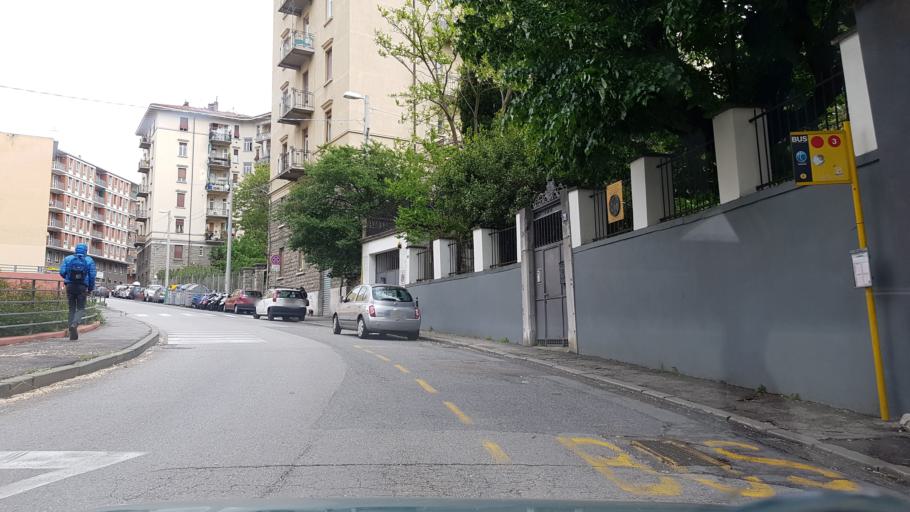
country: IT
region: Friuli Venezia Giulia
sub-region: Provincia di Trieste
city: Trieste
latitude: 45.6557
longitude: 13.7885
